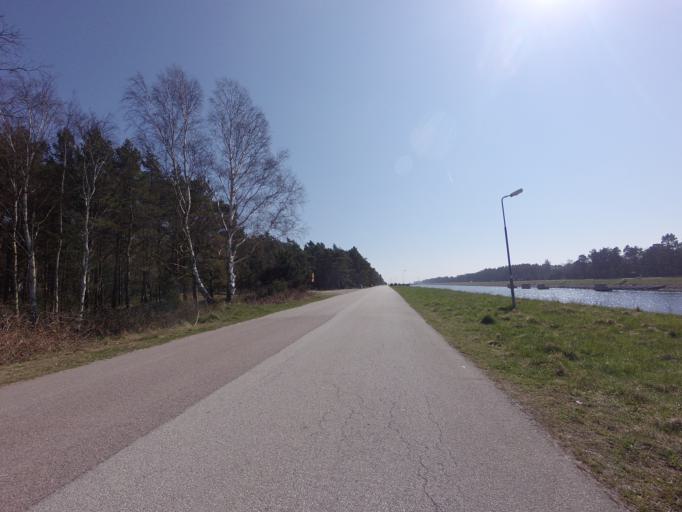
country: SE
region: Skane
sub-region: Vellinge Kommun
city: Ljunghusen
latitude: 55.4088
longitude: 12.9368
